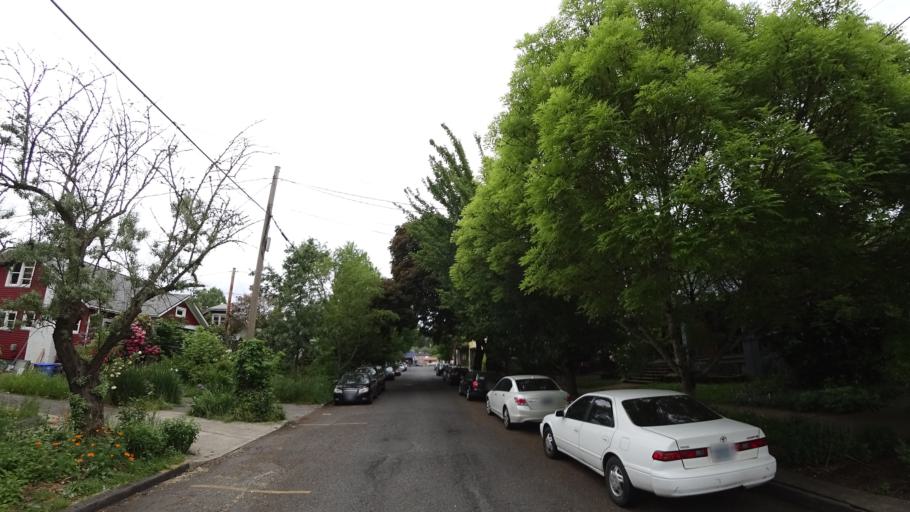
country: US
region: Oregon
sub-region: Multnomah County
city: Portland
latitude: 45.5111
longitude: -122.6212
